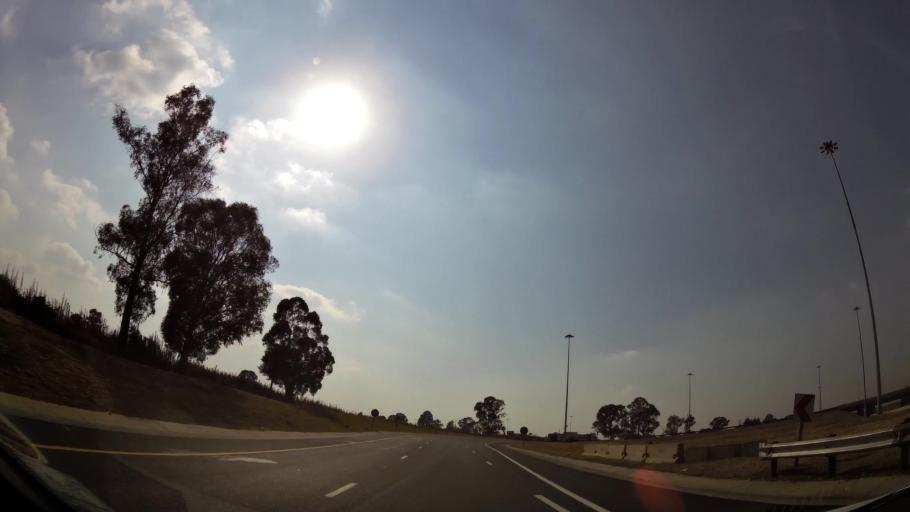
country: ZA
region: Gauteng
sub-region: Ekurhuleni Metropolitan Municipality
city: Brakpan
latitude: -26.1662
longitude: 28.3960
